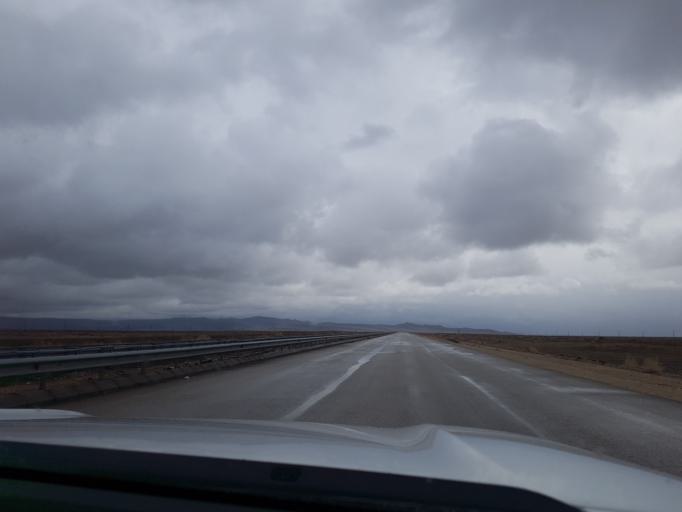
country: TM
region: Balkan
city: Balkanabat
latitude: 39.8284
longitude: 54.1345
